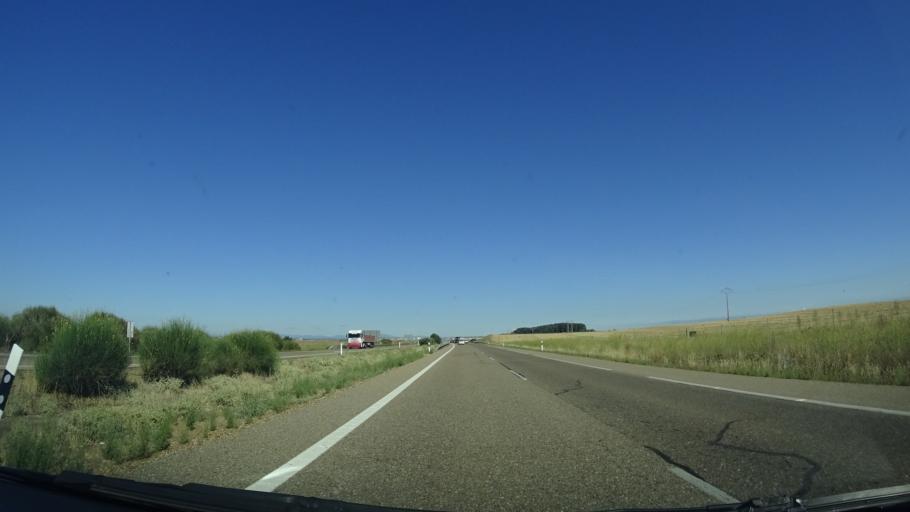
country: ES
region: Castille and Leon
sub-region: Provincia de Zamora
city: San Esteban del Molar
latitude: 41.9470
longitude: -5.5610
